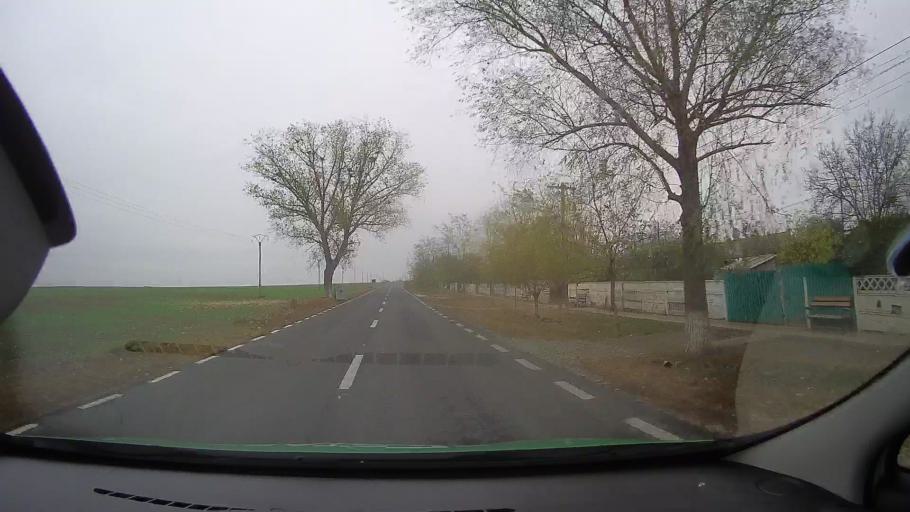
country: RO
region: Constanta
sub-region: Comuna Tortoman
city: Tortoman
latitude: 44.3501
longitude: 28.2173
